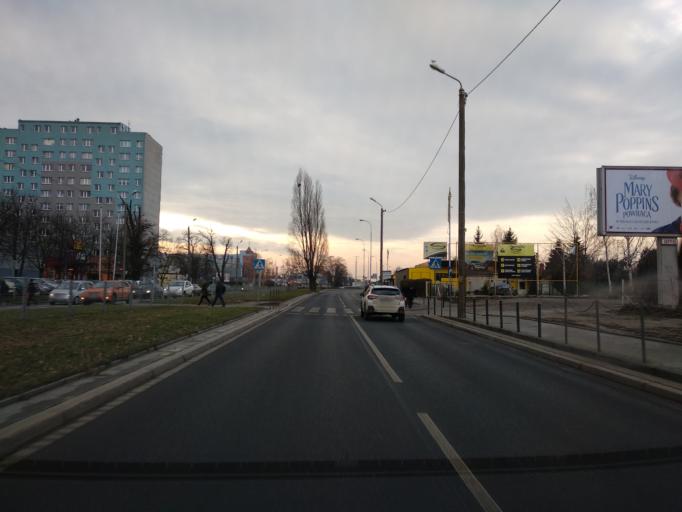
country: PL
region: Lower Silesian Voivodeship
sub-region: Powiat wroclawski
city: Wroclaw
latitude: 51.0858
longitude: 17.0351
